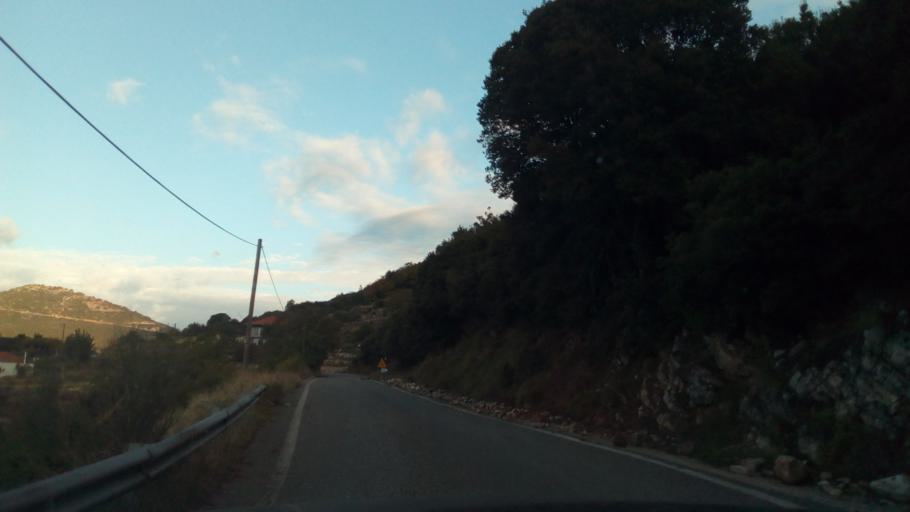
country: GR
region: West Greece
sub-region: Nomos Aitolias kai Akarnanias
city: Nafpaktos
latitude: 38.5239
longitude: 21.8374
